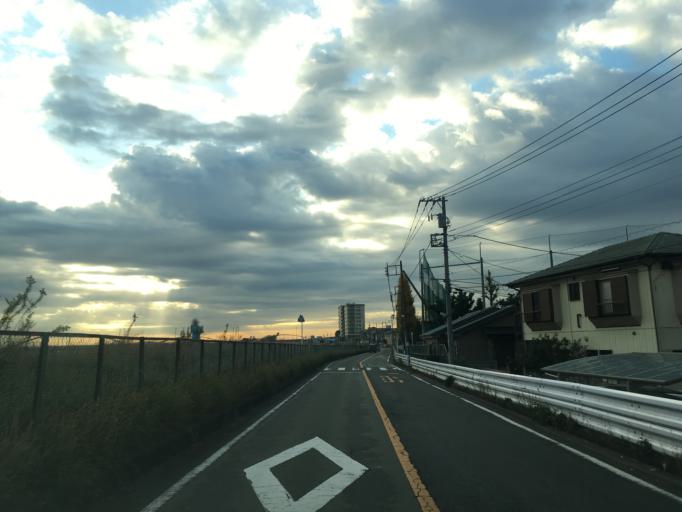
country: JP
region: Tokyo
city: Chofugaoka
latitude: 35.6456
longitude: 139.5203
